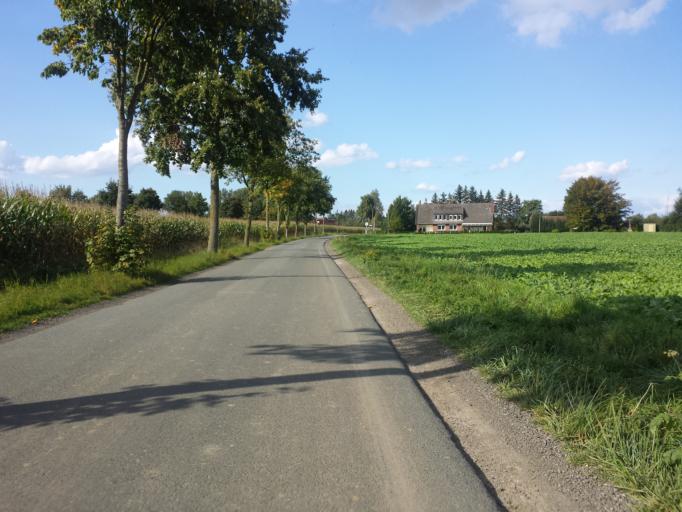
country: DE
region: North Rhine-Westphalia
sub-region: Regierungsbezirk Detmold
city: Langenberg
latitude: 51.7576
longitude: 8.3071
